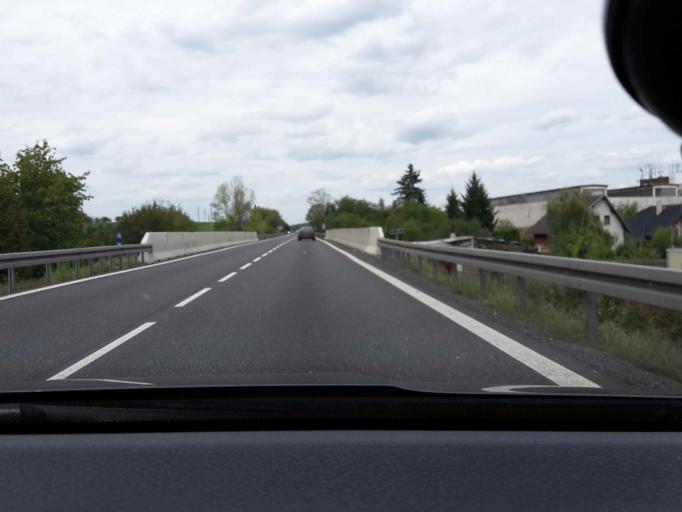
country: CZ
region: Central Bohemia
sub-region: Okres Benesov
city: Benesov
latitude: 49.7895
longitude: 14.6782
